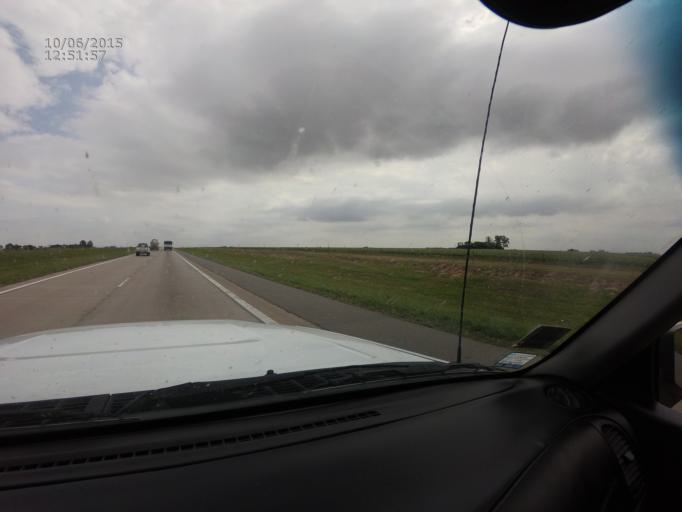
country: AR
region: Santa Fe
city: Armstrong
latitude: -32.8238
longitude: -61.5231
